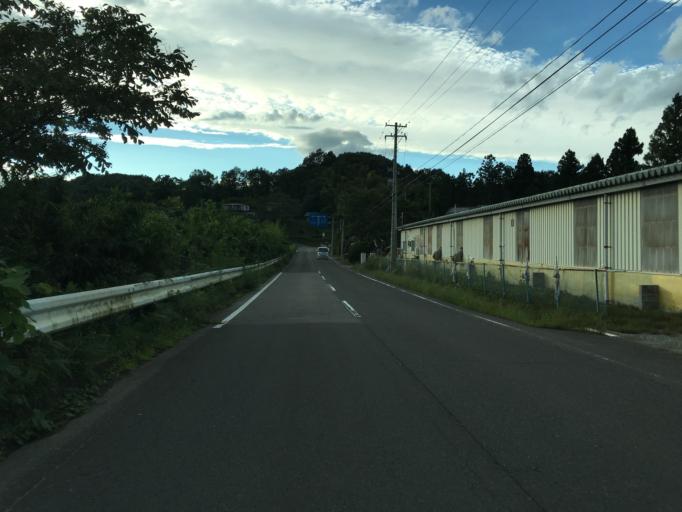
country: JP
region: Fukushima
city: Nihommatsu
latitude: 37.6337
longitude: 140.4944
